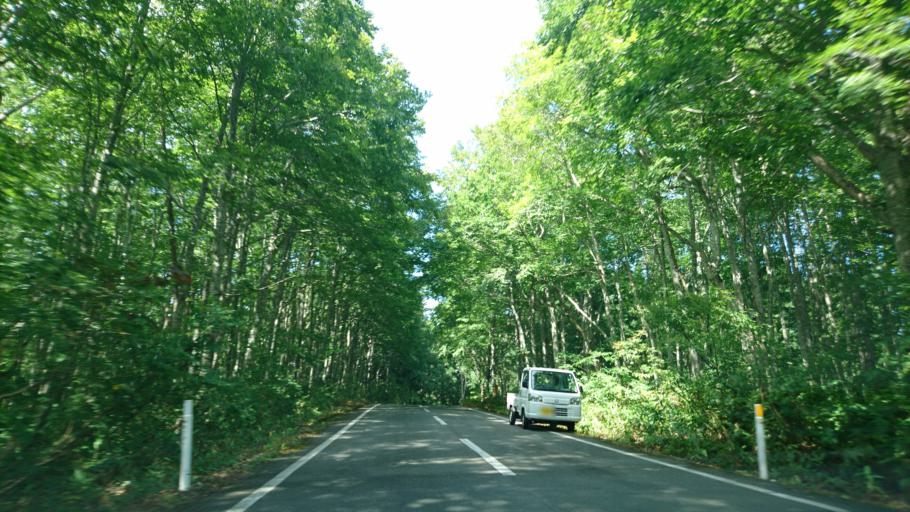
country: JP
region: Akita
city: Yuzawa
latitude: 38.9712
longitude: 140.7124
